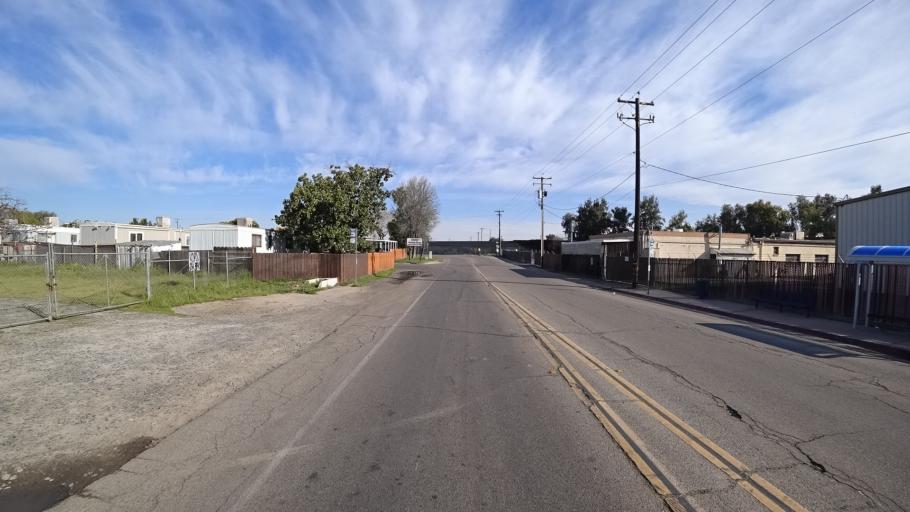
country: US
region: California
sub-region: Fresno County
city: West Park
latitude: 36.8026
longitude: -119.8806
